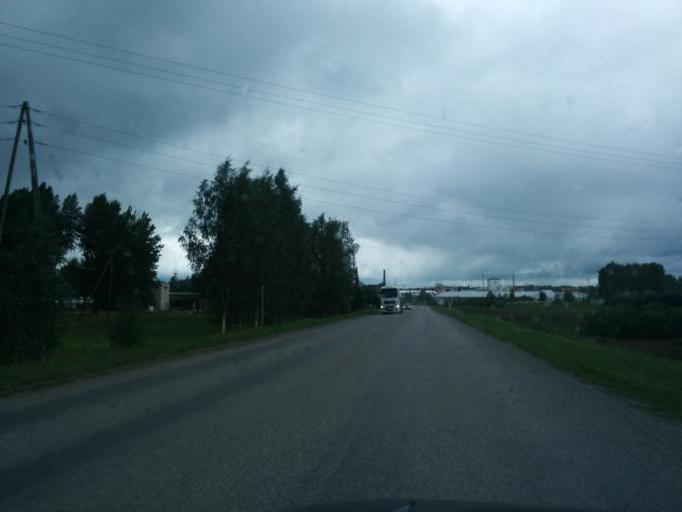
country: LV
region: Valmieras Rajons
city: Valmiera
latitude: 57.5160
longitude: 25.4553
